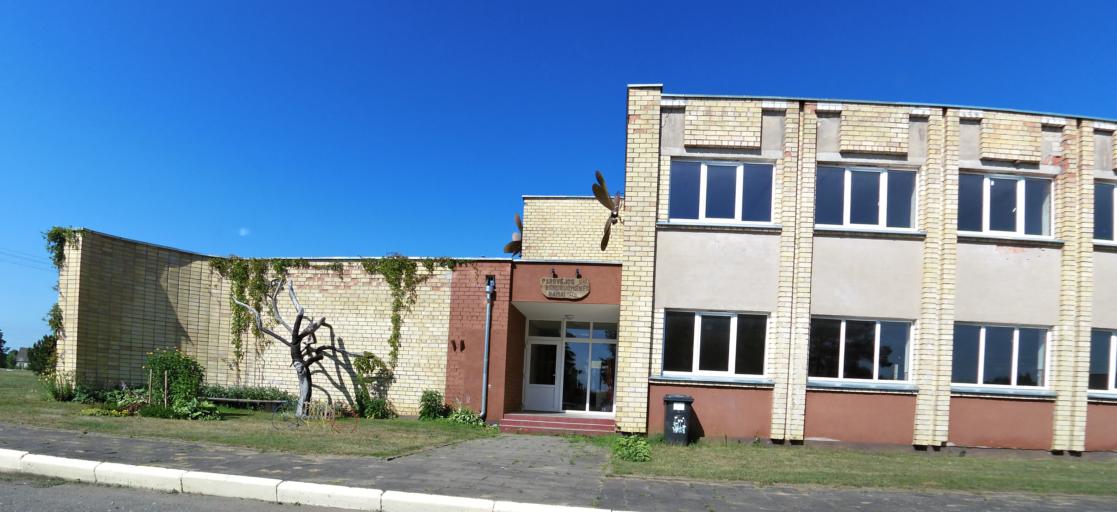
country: LT
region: Panevezys
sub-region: Birzai
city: Birzai
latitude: 56.2456
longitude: 24.8576
